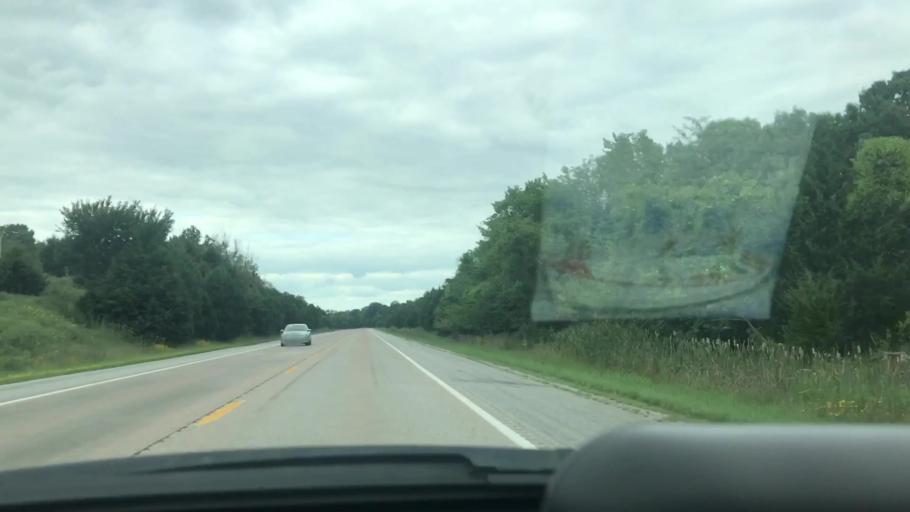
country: US
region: Missouri
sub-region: Benton County
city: Warsaw
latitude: 38.1988
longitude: -93.3254
